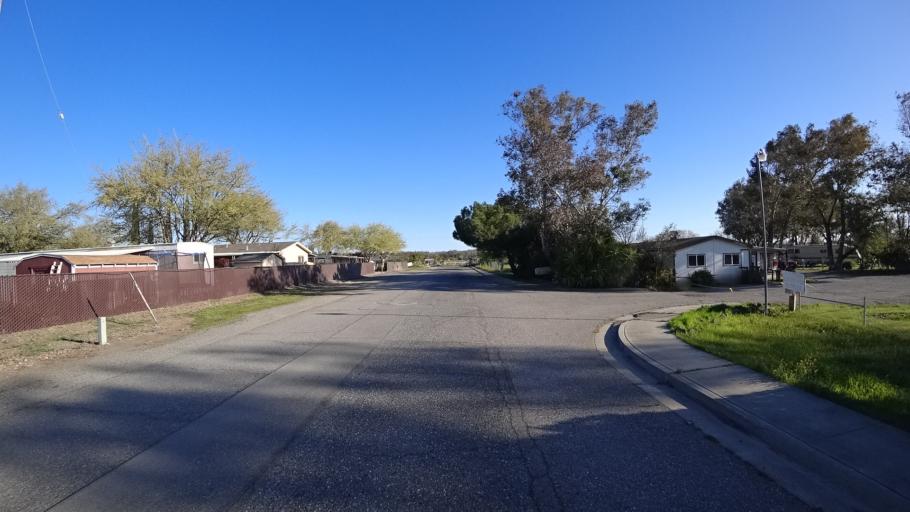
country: US
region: California
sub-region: Glenn County
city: Orland
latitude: 39.7537
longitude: -122.2089
